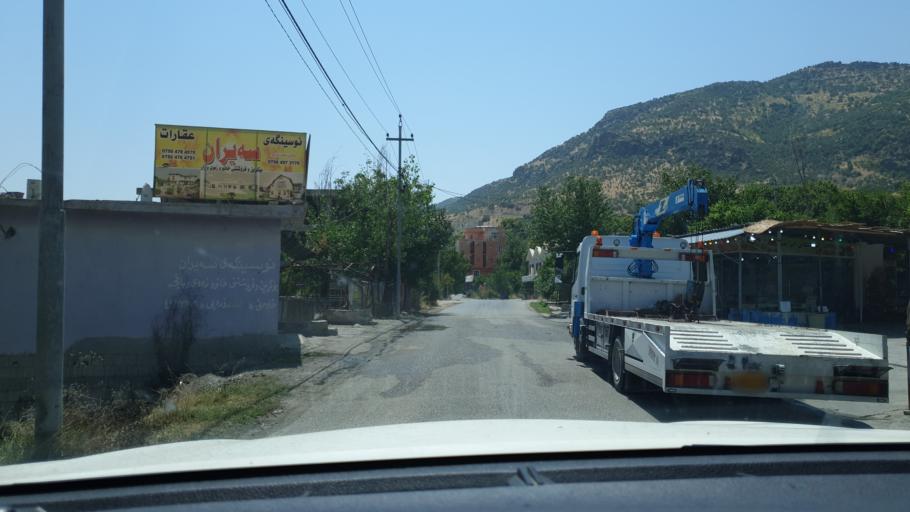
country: IQ
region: Arbil
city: Nahiyat Hiran
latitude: 36.2818
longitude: 44.4944
